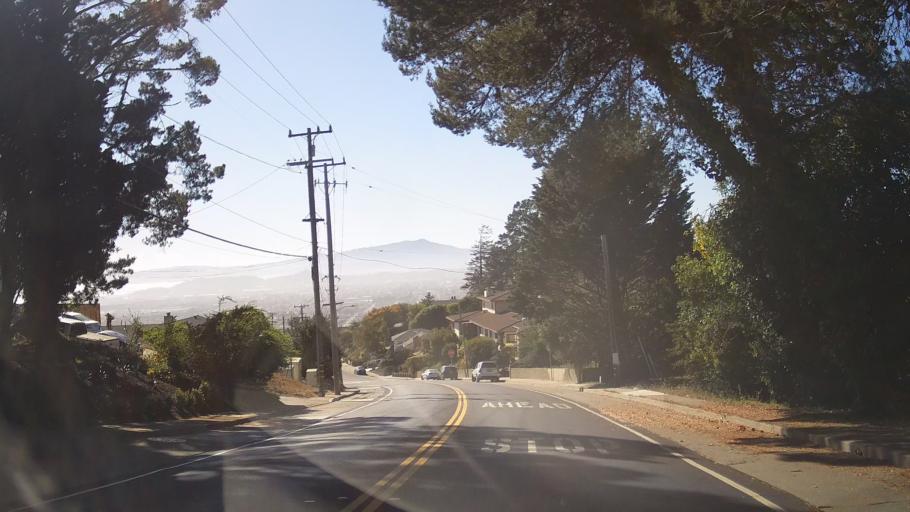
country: US
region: California
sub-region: Contra Costa County
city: El Cerrito
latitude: 37.9298
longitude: -122.3032
